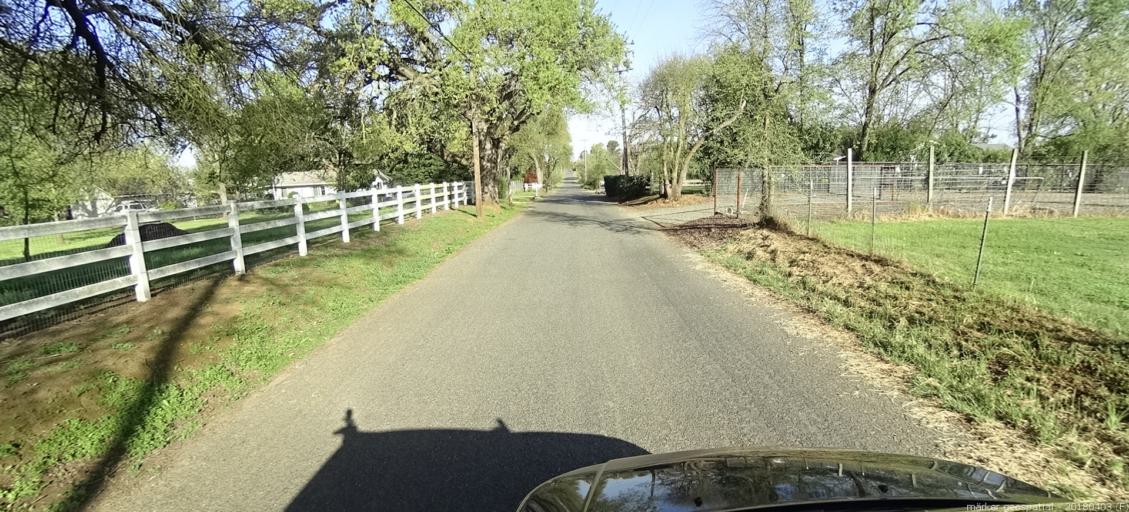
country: US
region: California
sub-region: Sacramento County
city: Wilton
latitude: 38.4409
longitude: -121.1956
